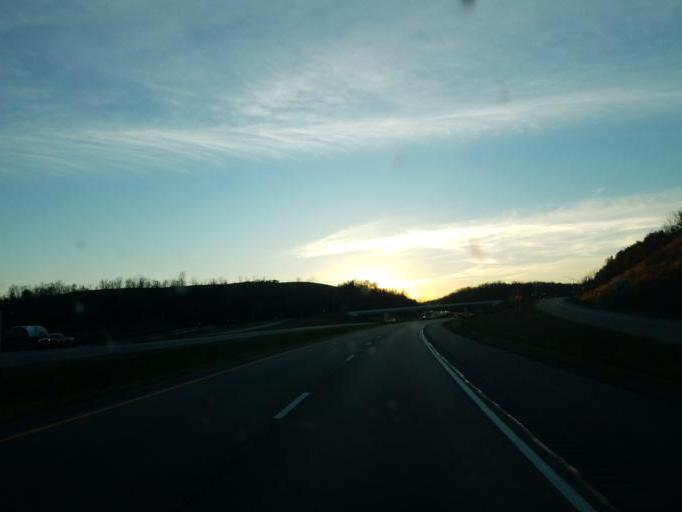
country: US
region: Ohio
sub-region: Belmont County
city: Barnesville
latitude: 40.0581
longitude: -81.1540
